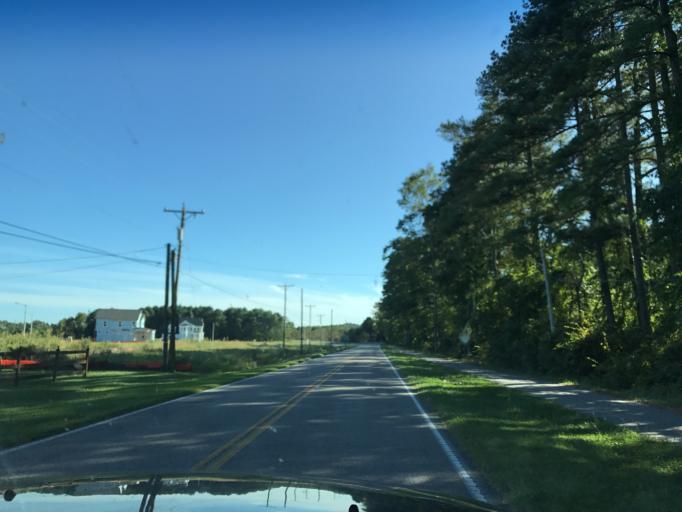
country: US
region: Virginia
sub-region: City of Portsmouth
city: Portsmouth Heights
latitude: 36.6962
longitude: -76.3573
